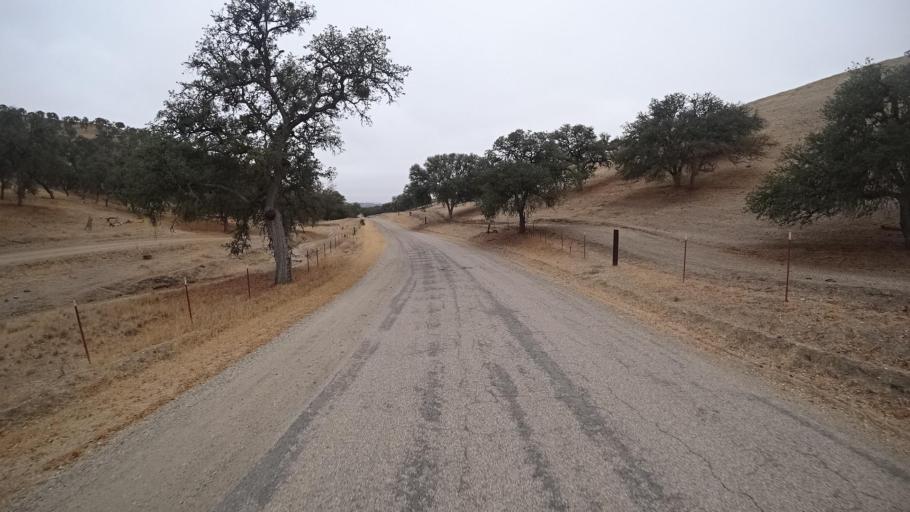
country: US
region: California
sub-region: San Luis Obispo County
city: San Miguel
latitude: 35.8784
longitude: -120.7469
